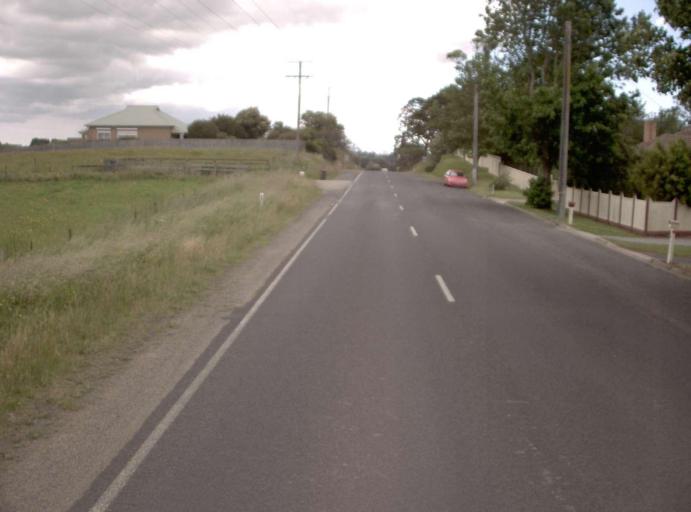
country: AU
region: Victoria
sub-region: Baw Baw
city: Warragul
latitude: -38.1365
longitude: 145.9349
